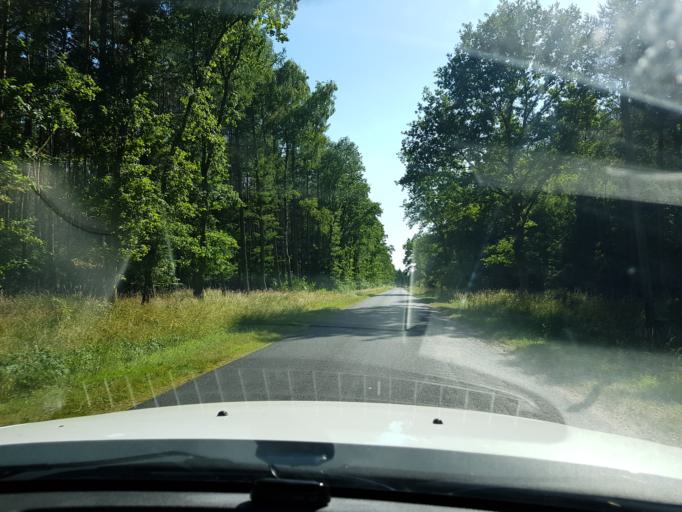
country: PL
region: West Pomeranian Voivodeship
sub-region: Powiat swidwinski
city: Slawoborze
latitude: 53.9062
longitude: 15.7459
